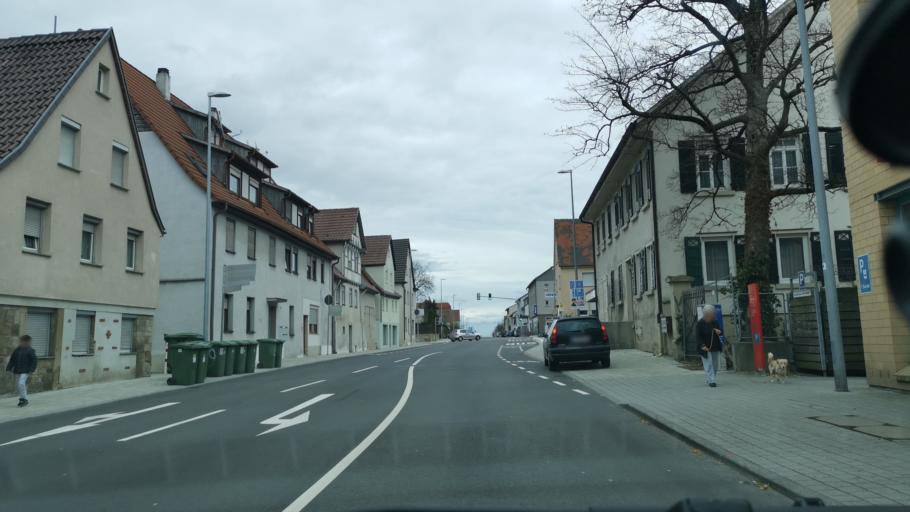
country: DE
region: Baden-Wuerttemberg
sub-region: Regierungsbezirk Stuttgart
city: Markgroningen
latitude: 48.9051
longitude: 9.0846
